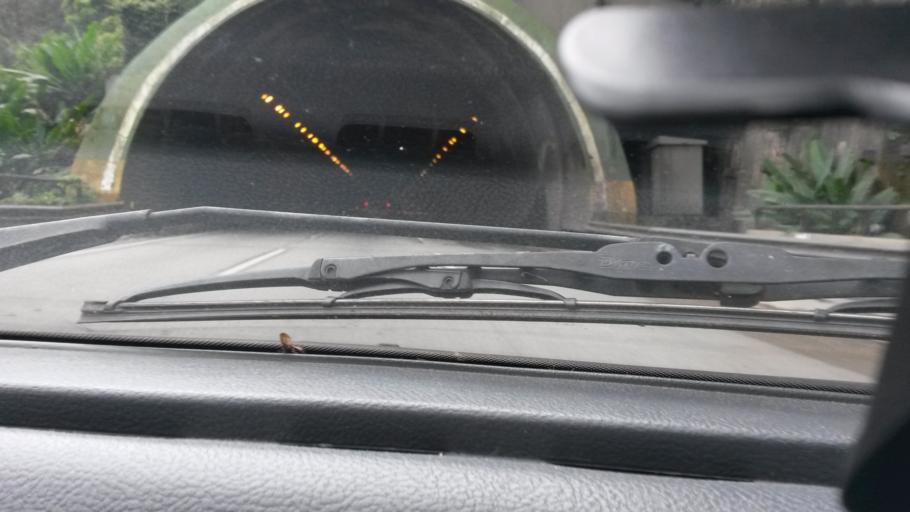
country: BR
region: Sao Paulo
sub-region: Cubatao
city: Cubatao
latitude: -23.9113
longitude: -46.5189
